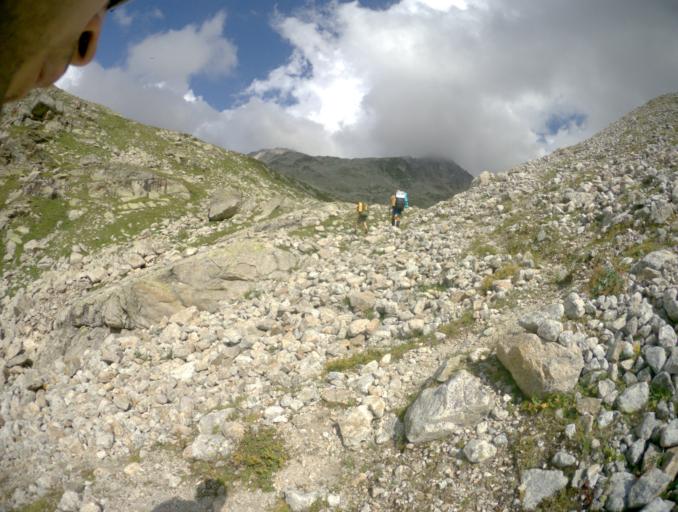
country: RU
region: Karachayevo-Cherkesiya
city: Uchkulan
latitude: 43.2836
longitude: 42.0958
